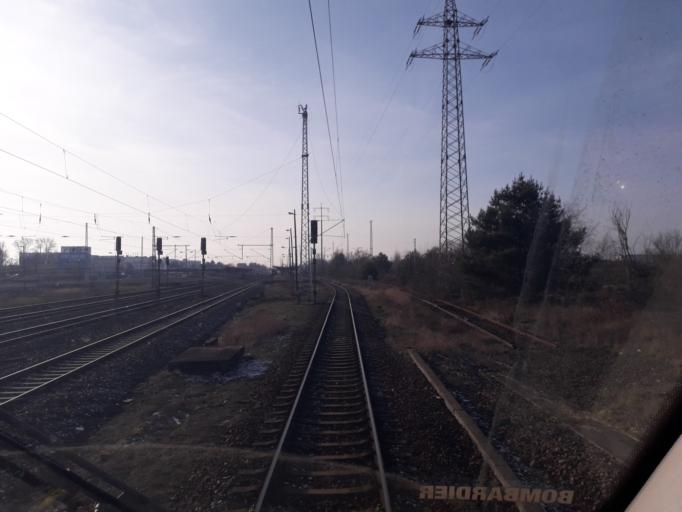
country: DE
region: Brandenburg
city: Schonefeld
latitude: 52.3935
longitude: 13.5167
